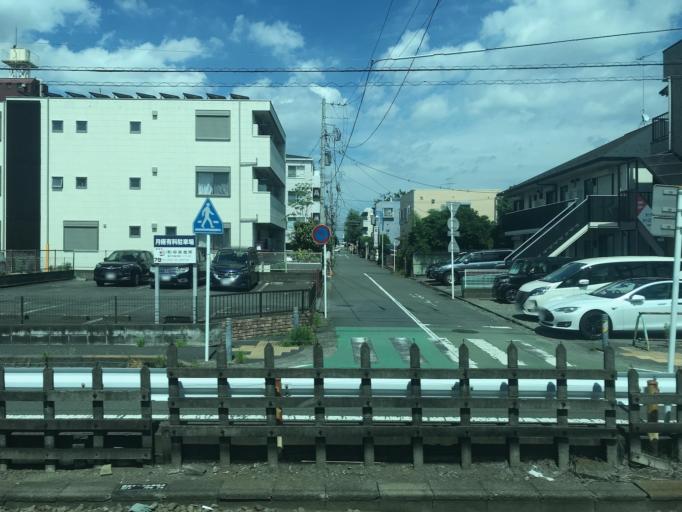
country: JP
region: Kanagawa
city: Fujisawa
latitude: 35.3944
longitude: 139.4673
